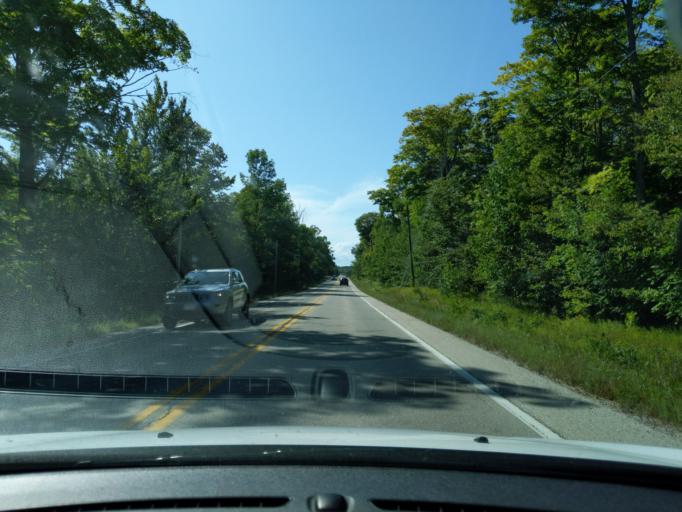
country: US
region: Michigan
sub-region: Delta County
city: Escanaba
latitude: 45.2594
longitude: -87.0353
